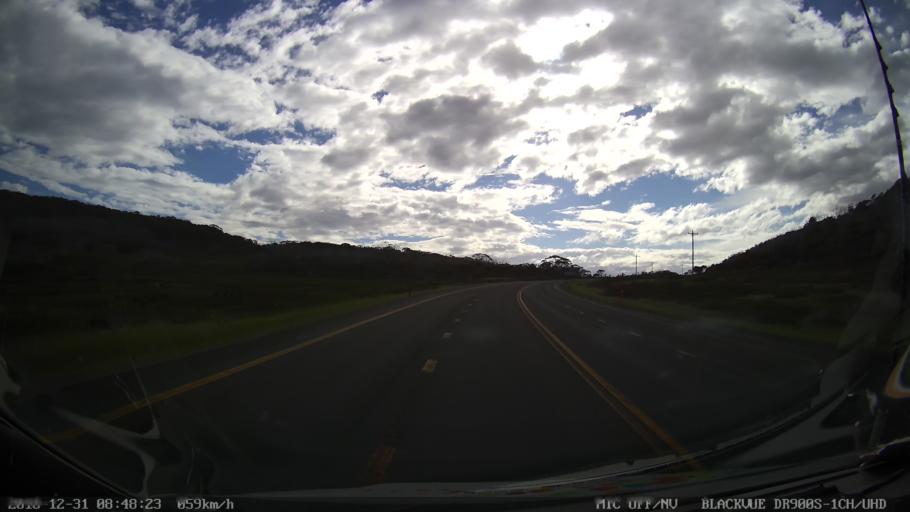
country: AU
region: New South Wales
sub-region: Snowy River
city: Jindabyne
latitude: -36.3586
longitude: 148.4957
